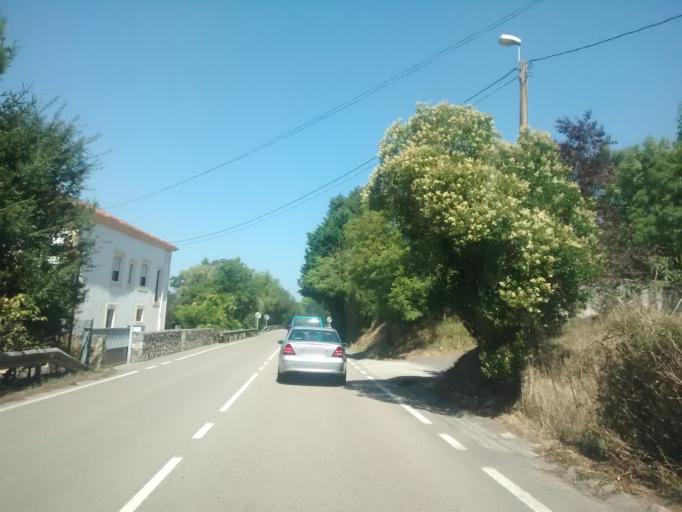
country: ES
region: Cantabria
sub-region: Provincia de Cantabria
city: San Miguel de Meruelo
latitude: 43.4649
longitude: -3.5854
